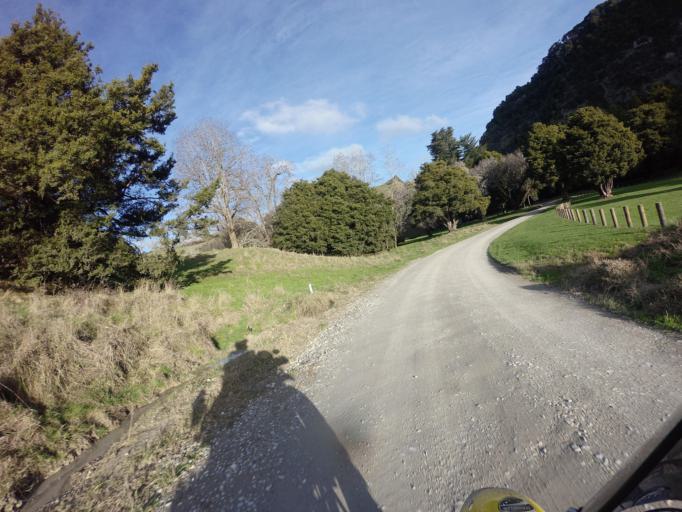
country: NZ
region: Hawke's Bay
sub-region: Wairoa District
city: Wairoa
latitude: -38.7331
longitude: 177.5867
